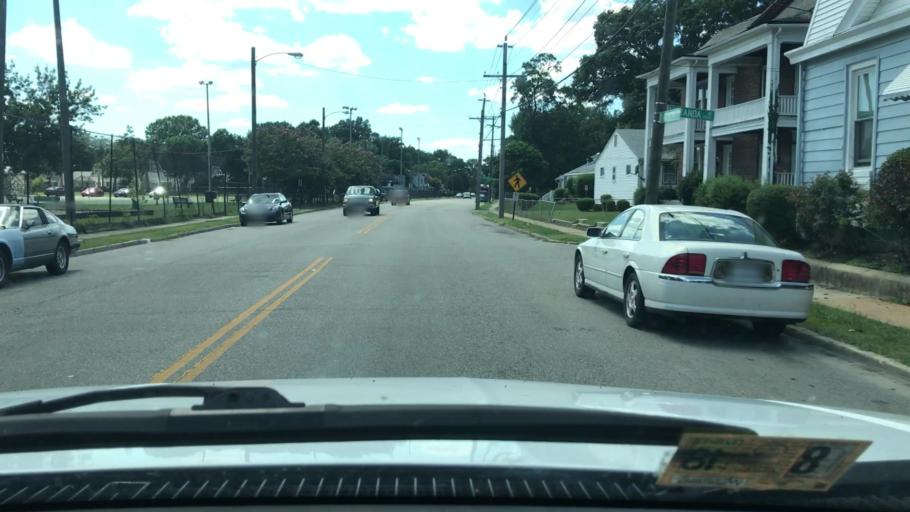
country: US
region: Virginia
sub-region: Henrico County
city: East Highland Park
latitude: 37.5703
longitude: -77.4217
